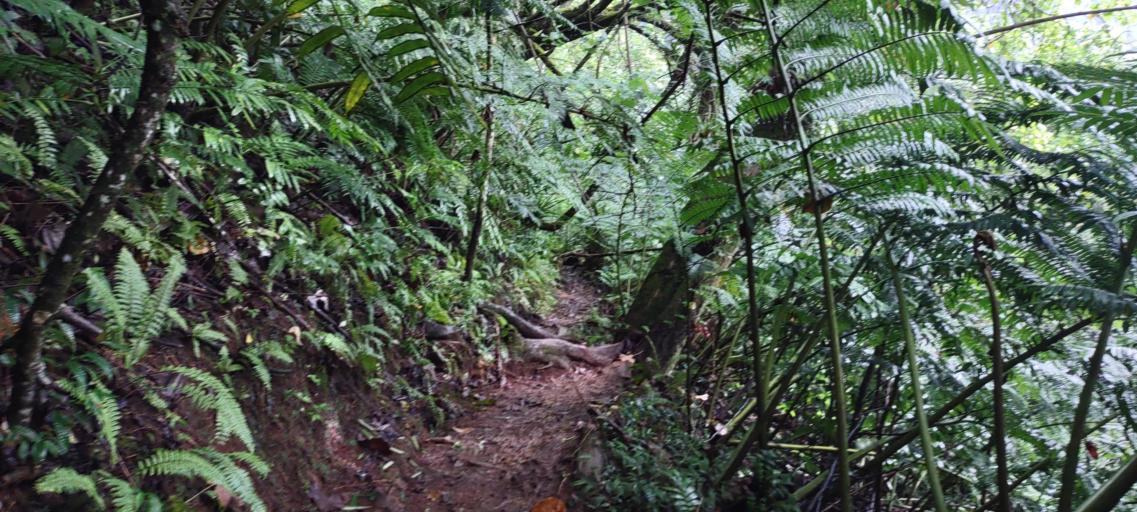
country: PF
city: Paopao
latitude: -17.5422
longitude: -149.8282
